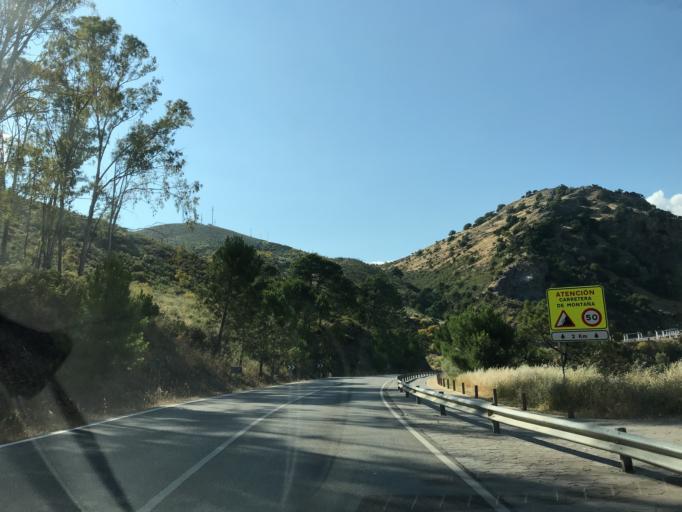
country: ES
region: Andalusia
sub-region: Provincia de Malaga
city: Benahavis
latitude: 36.5083
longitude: -5.0345
